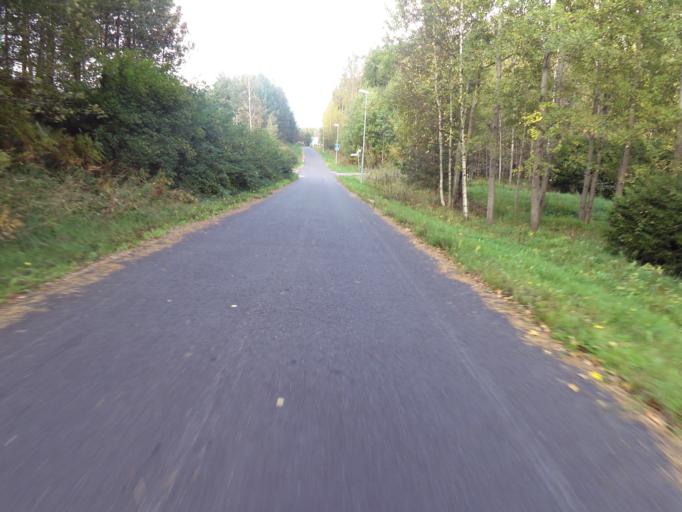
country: FI
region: Uusimaa
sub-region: Helsinki
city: Kauniainen
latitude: 60.2569
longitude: 24.7205
